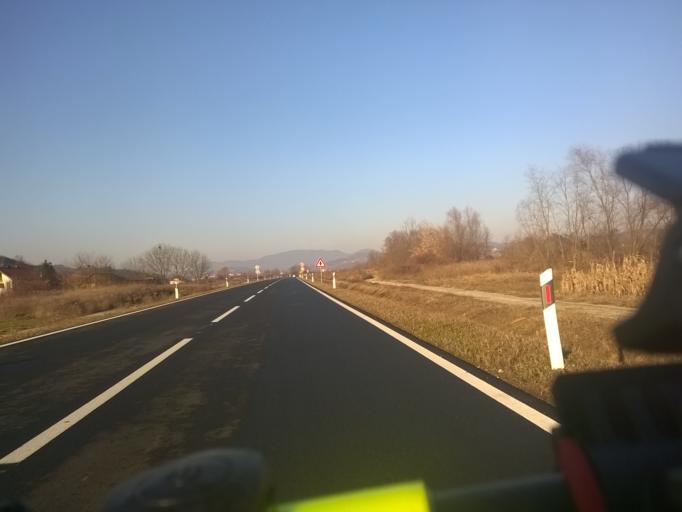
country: HR
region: Krapinsko-Zagorska
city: Zabok
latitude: 46.0546
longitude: 15.9129
